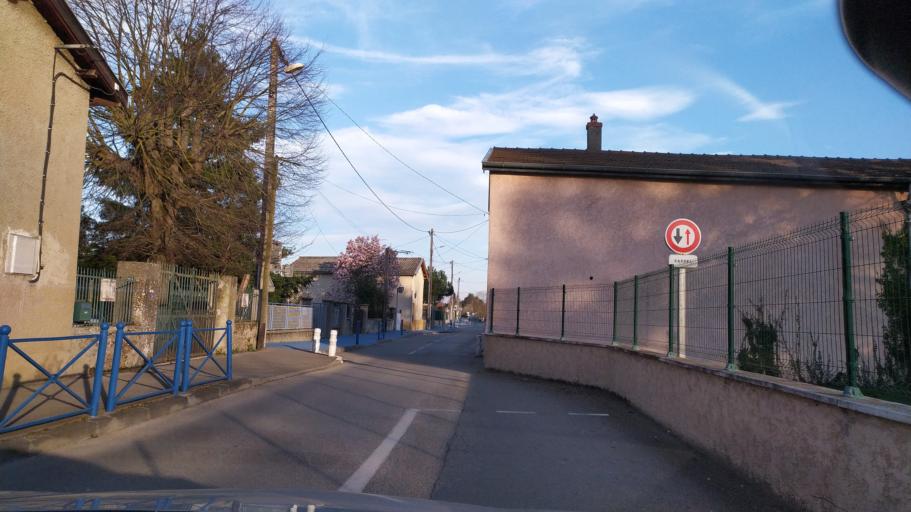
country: FR
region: Rhone-Alpes
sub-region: Departement de l'Isere
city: Charvieu-Chavagneux
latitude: 45.7270
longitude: 5.1476
